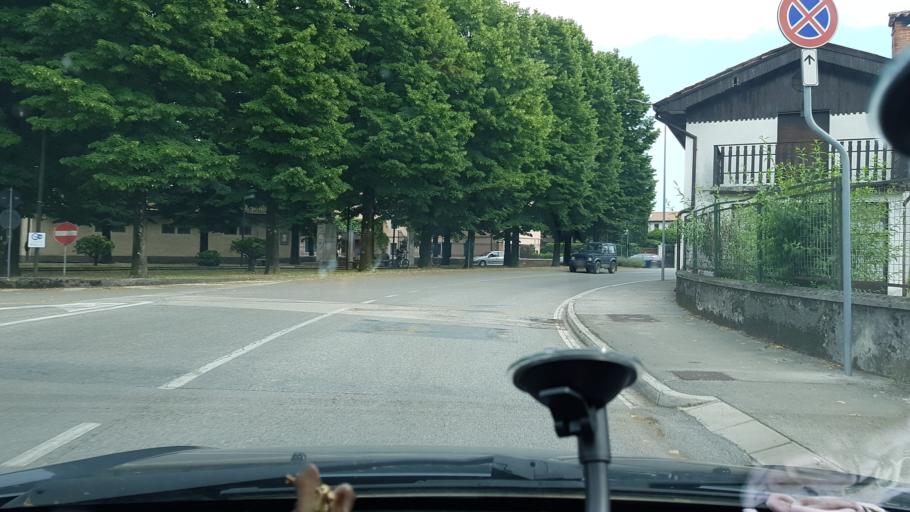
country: IT
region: Friuli Venezia Giulia
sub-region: Provincia di Gorizia
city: San Lorenzo Isontino
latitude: 45.9328
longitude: 13.5256
